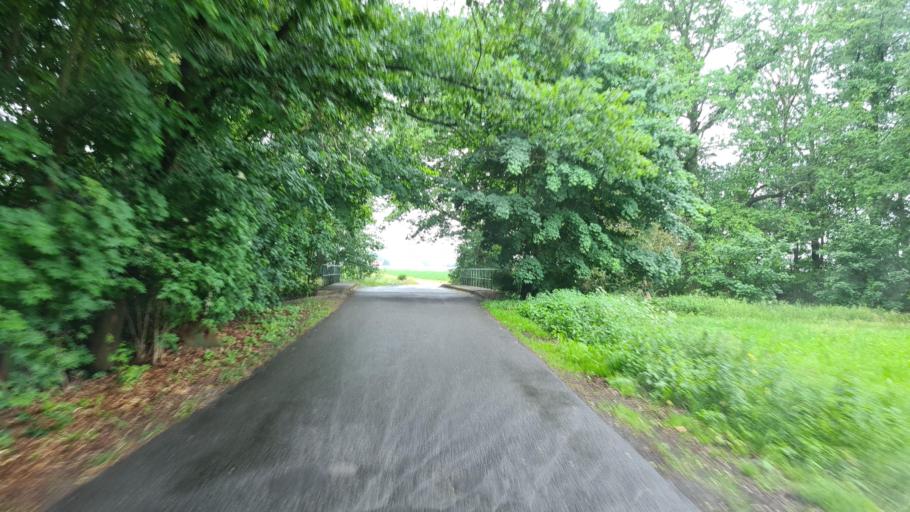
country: DE
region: Brandenburg
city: Lindenau
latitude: 51.3919
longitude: 13.7234
